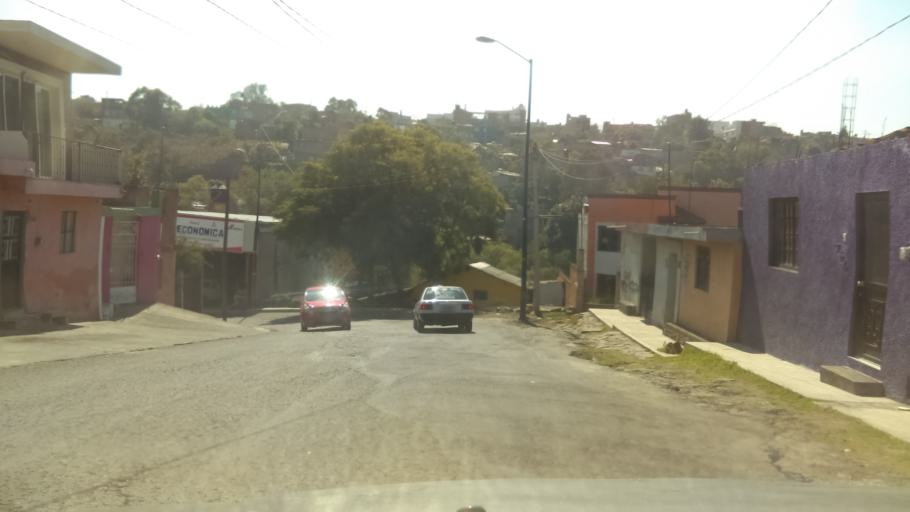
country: MX
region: Michoacan
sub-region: Morelia
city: Montana Monarca (Punta Altozano)
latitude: 19.6686
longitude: -101.1896
